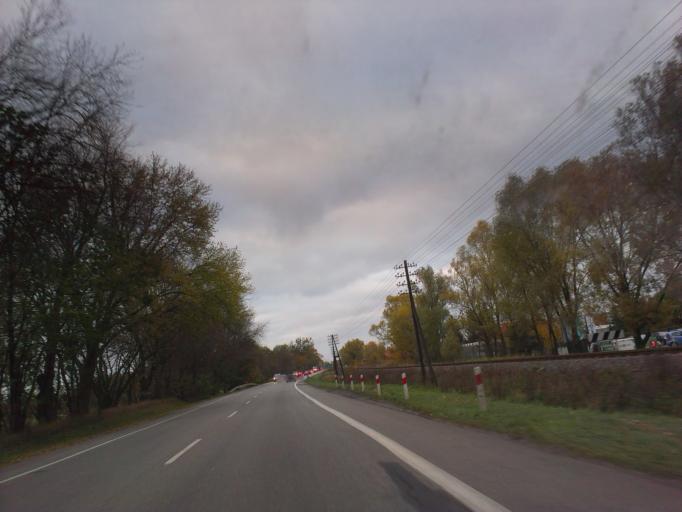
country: PL
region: Kujawsko-Pomorskie
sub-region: Powiat torunski
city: Lysomice
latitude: 53.0792
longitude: 18.6185
